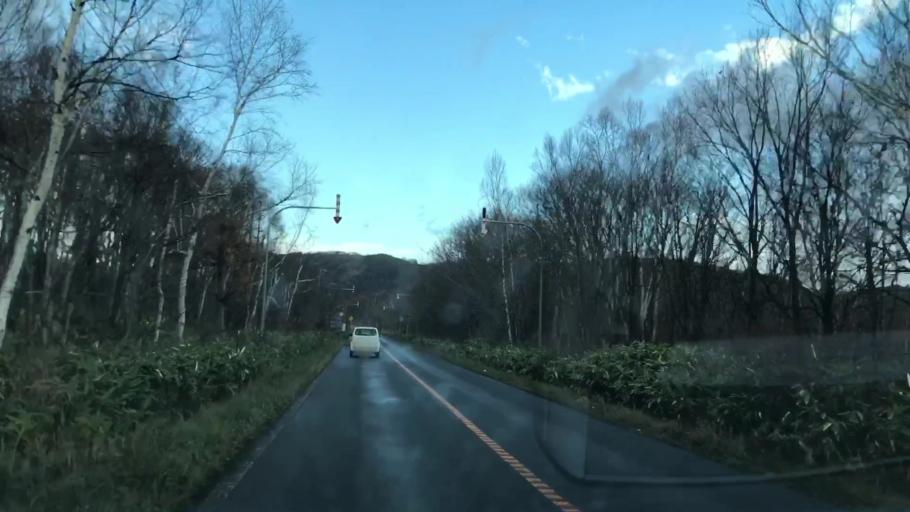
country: JP
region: Hokkaido
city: Yoichi
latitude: 43.3259
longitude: 140.5007
